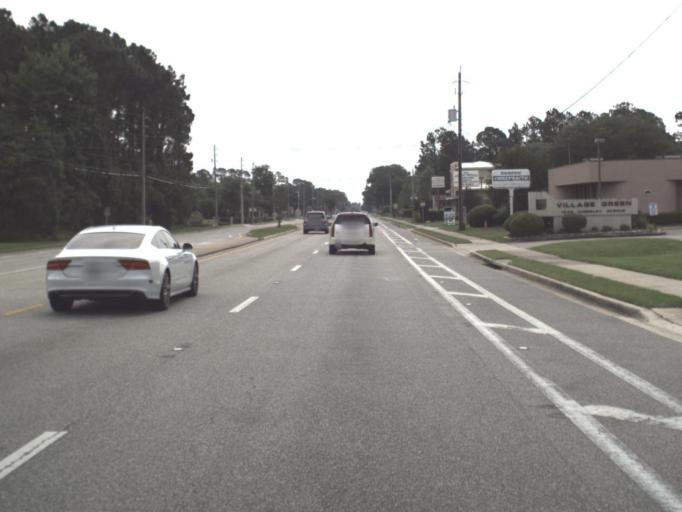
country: US
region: Florida
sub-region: Clay County
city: Bellair-Meadowbrook Terrace
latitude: 30.1650
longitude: -81.7286
